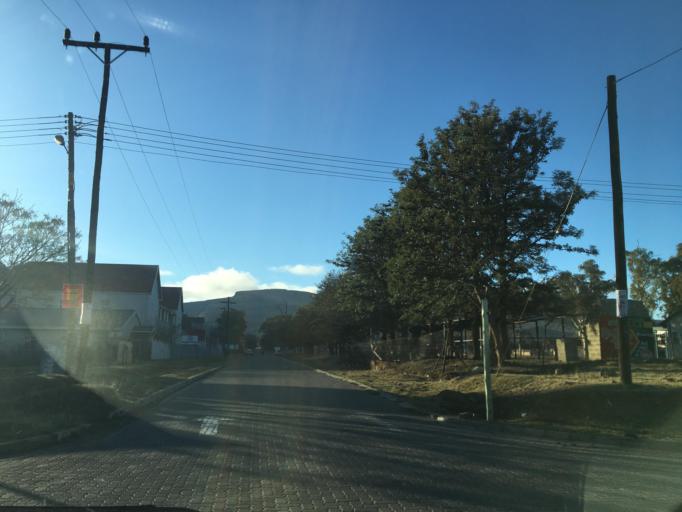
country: ZA
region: Eastern Cape
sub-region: Chris Hani District Municipality
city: Cala
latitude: -31.5253
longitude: 27.6978
